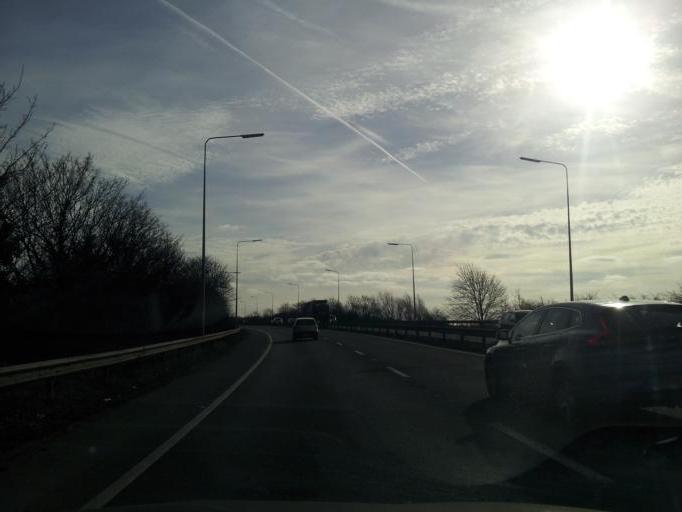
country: GB
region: England
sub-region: Central Bedfordshire
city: Biggleswade
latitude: 52.0779
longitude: -0.2670
